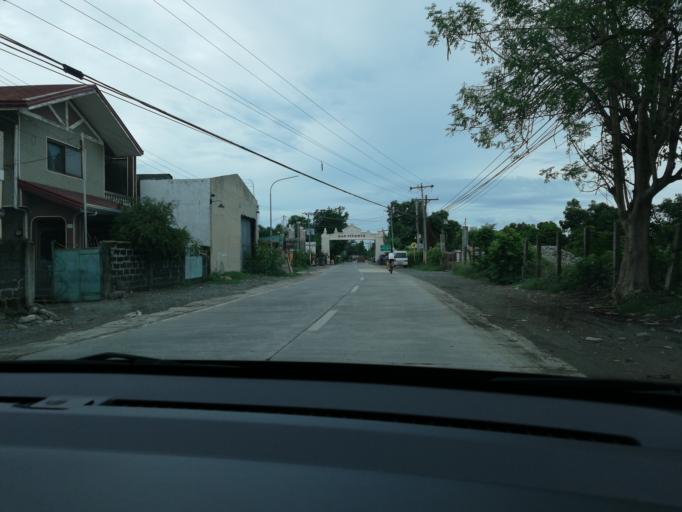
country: PH
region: Ilocos
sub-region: Province of Ilocos Sur
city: Bantay
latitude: 17.5839
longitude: 120.3835
